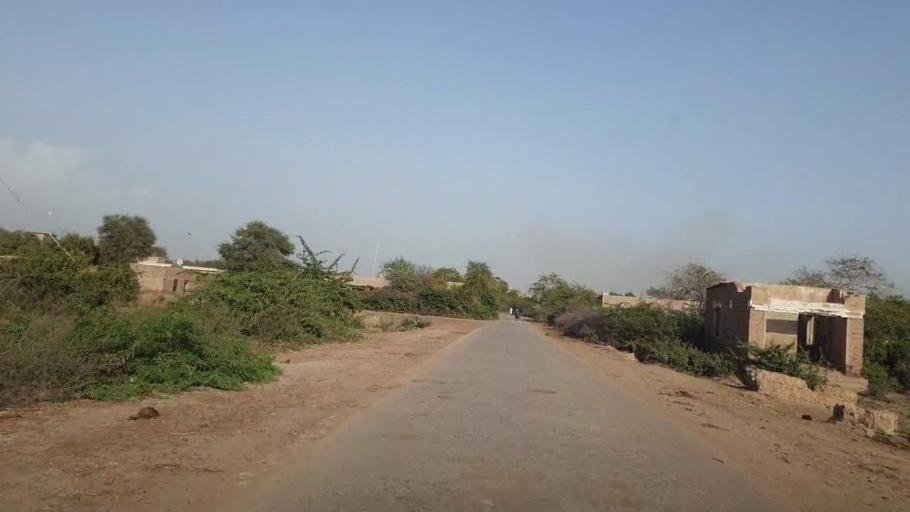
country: PK
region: Sindh
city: Tando Ghulam Ali
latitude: 25.0876
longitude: 68.8697
